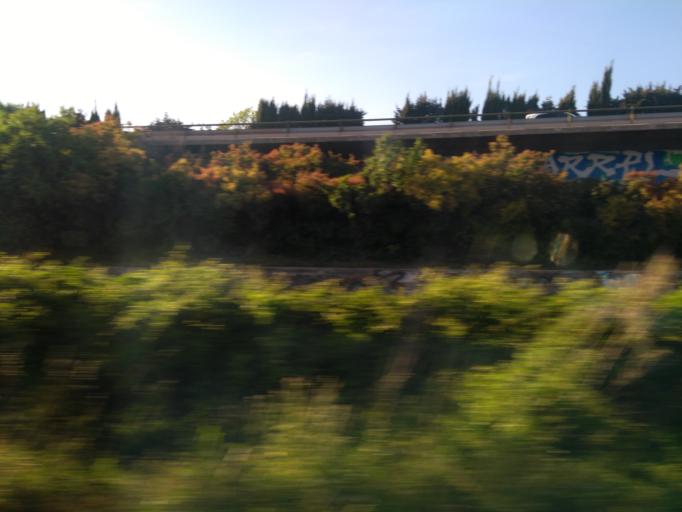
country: FR
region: Provence-Alpes-Cote d'Azur
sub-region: Departement des Bouches-du-Rhone
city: Aubagne
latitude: 43.2892
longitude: 5.5519
